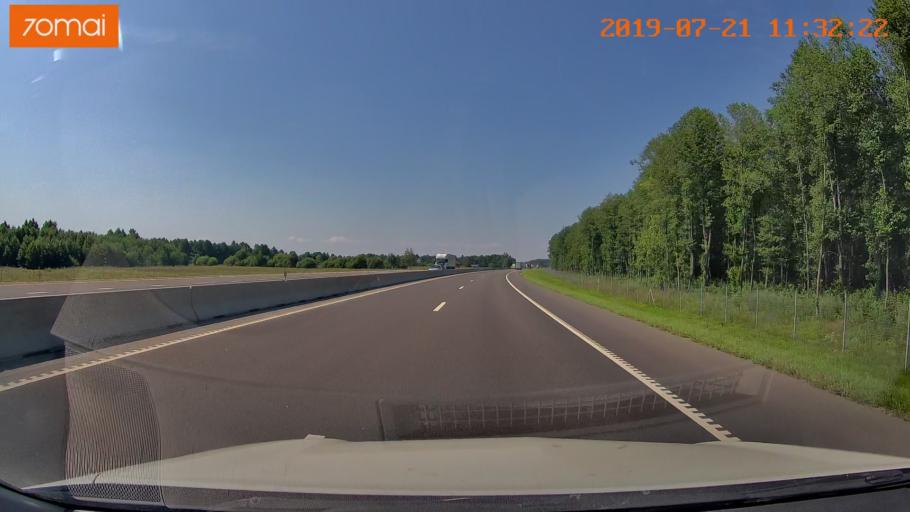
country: BY
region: Minsk
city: Valozhyn
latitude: 54.0035
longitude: 26.3750
